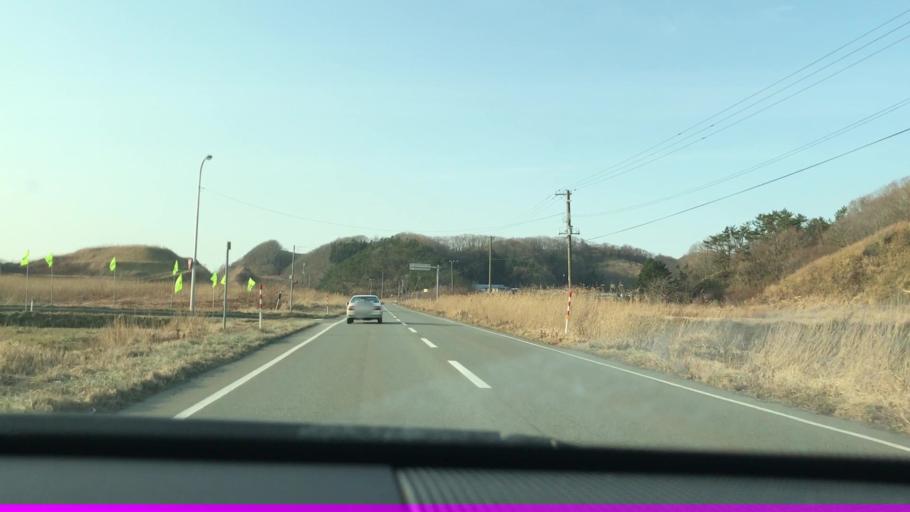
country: JP
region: Hokkaido
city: Shizunai-furukawacho
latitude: 42.2299
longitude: 142.6137
